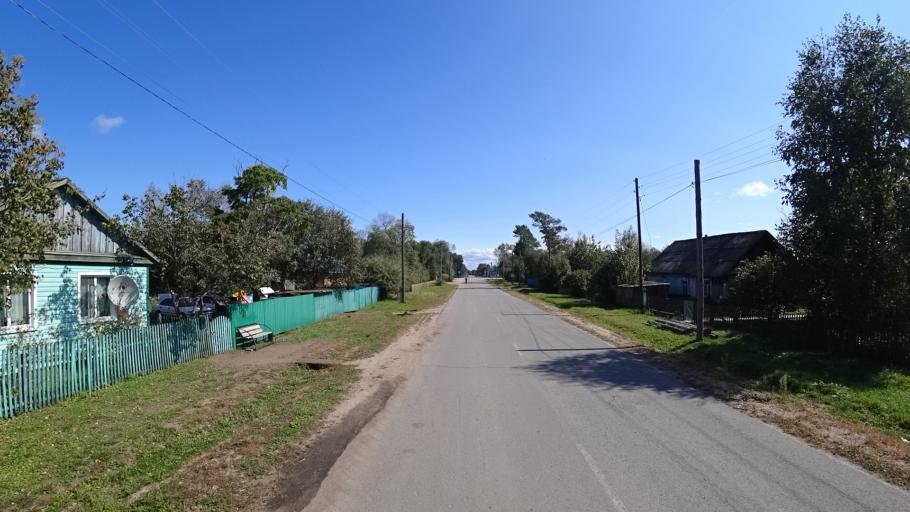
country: RU
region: Amur
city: Arkhara
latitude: 49.4034
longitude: 130.1358
